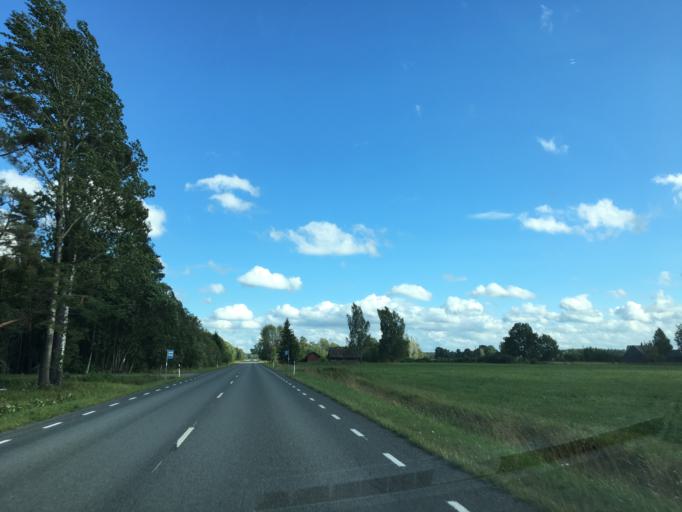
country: EE
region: Paernumaa
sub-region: Vaendra vald (alev)
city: Vandra
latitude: 58.5874
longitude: 25.1683
